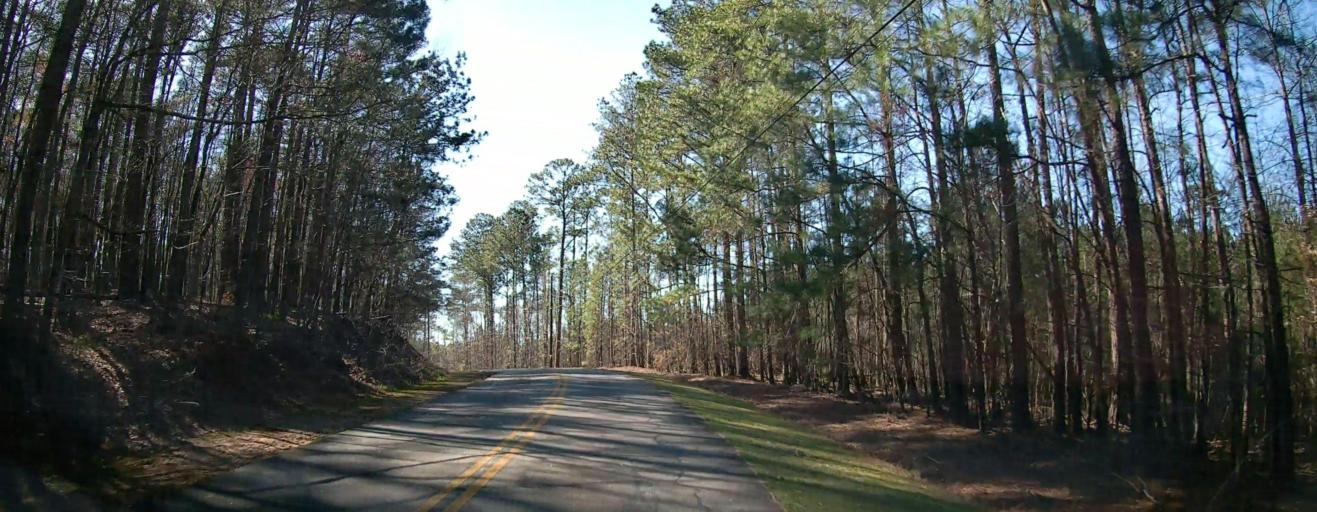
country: US
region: Georgia
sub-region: Butts County
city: Indian Springs
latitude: 33.2534
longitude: -83.9313
